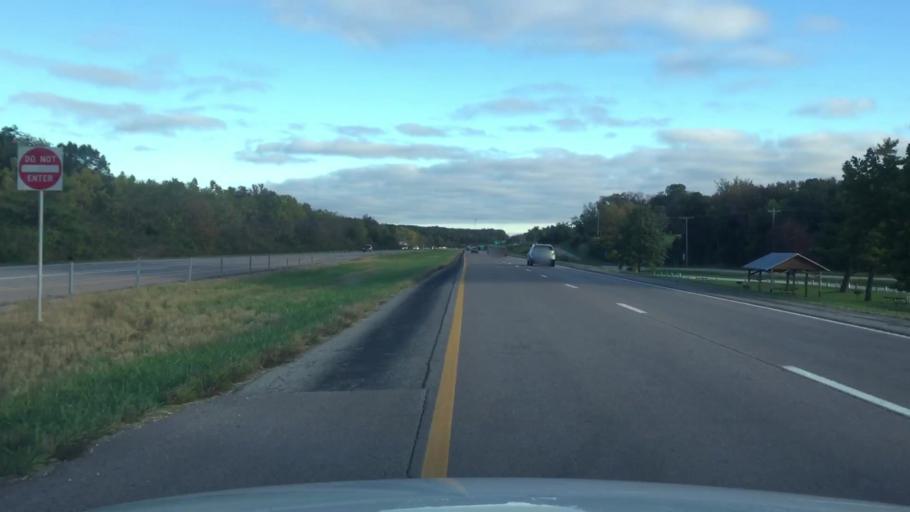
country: US
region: Missouri
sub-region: Boone County
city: Ashland
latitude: 38.8108
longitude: -92.2513
